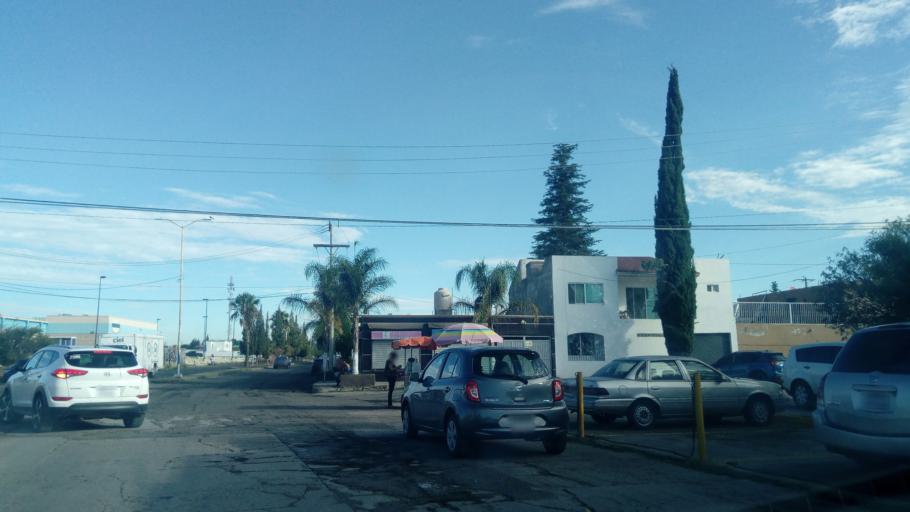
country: MX
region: Durango
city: Victoria de Durango
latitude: 24.0553
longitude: -104.6095
